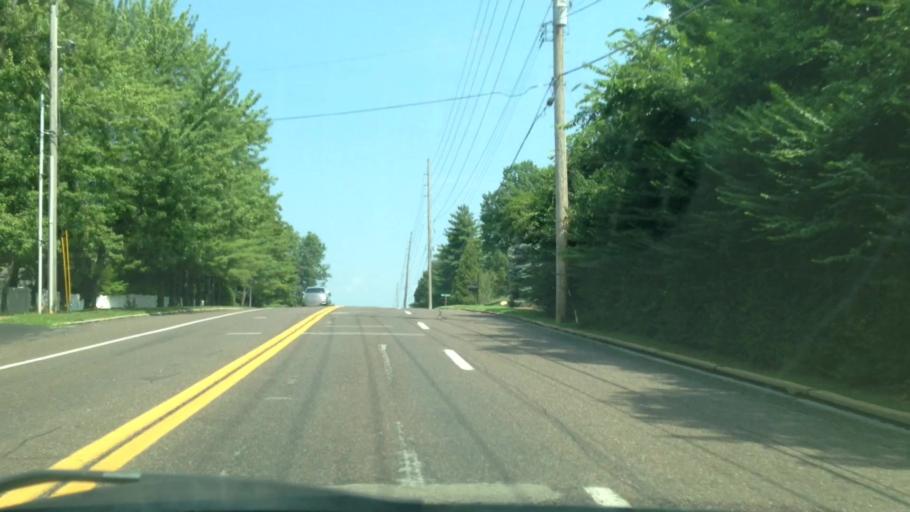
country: US
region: Missouri
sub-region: Saint Louis County
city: Des Peres
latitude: 38.5925
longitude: -90.4441
